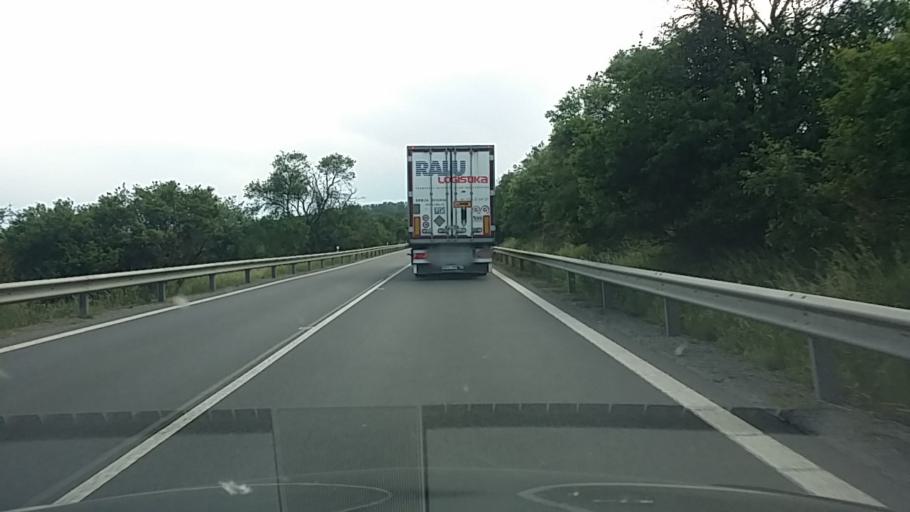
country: SK
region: Banskobystricky
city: Krupina
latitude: 48.3228
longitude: 19.0575
